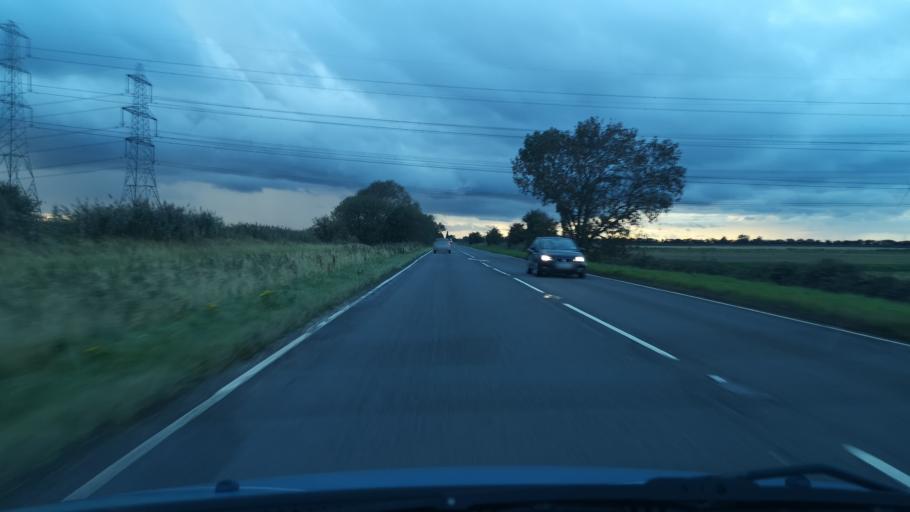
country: GB
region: England
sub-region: North Lincolnshire
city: Gunness
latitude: 53.5770
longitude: -0.7584
